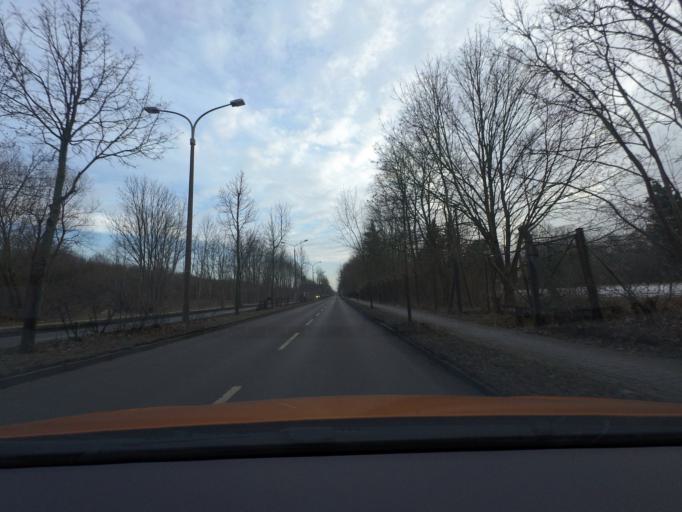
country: DE
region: Berlin
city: Blankenfelde
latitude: 52.6091
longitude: 13.3982
